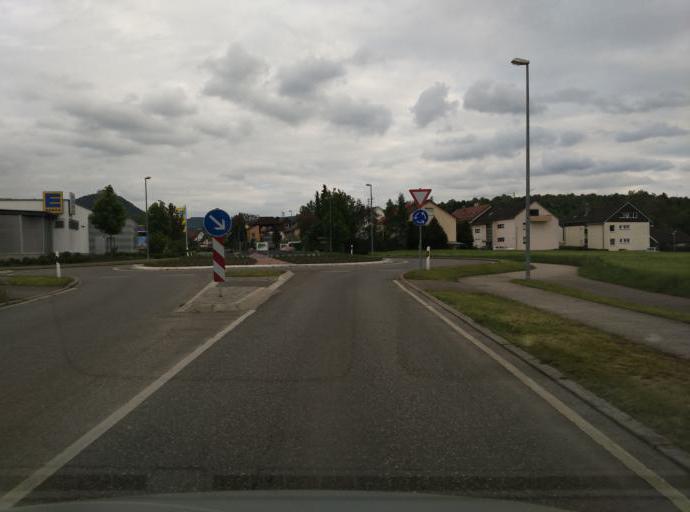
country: DE
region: Baden-Wuerttemberg
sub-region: Regierungsbezirk Stuttgart
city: Frickenhausen
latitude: 48.5848
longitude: 9.3657
